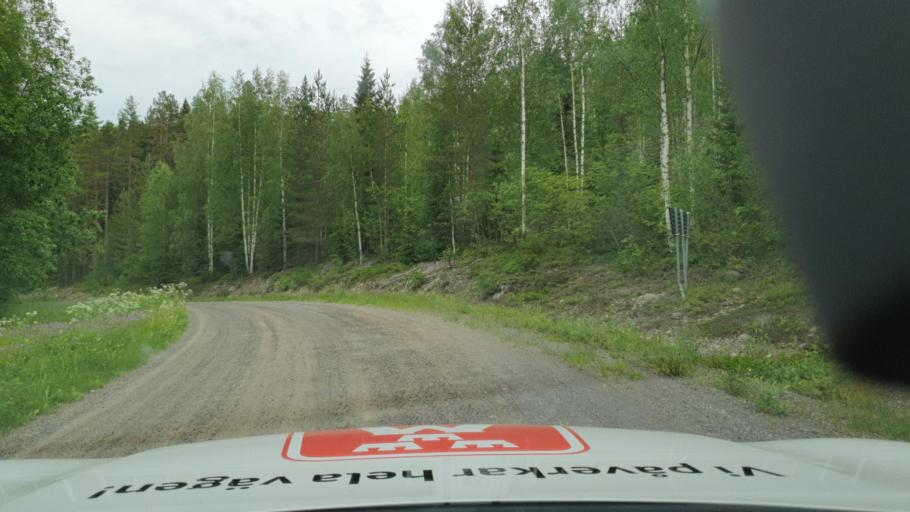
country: SE
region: Vaesterbotten
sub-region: Robertsfors Kommun
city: Robertsfors
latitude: 64.2098
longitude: 20.6945
